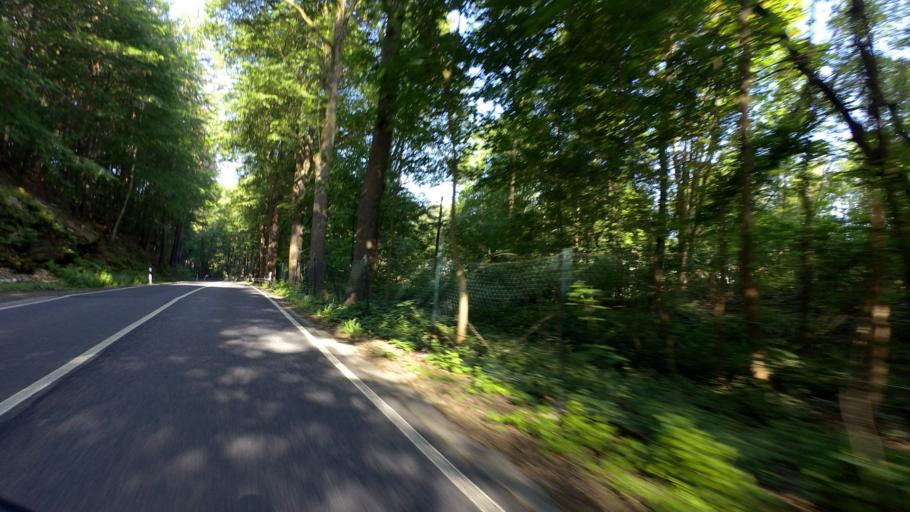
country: DE
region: Saxony
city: Bad Schandau
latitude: 50.9279
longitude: 14.1605
